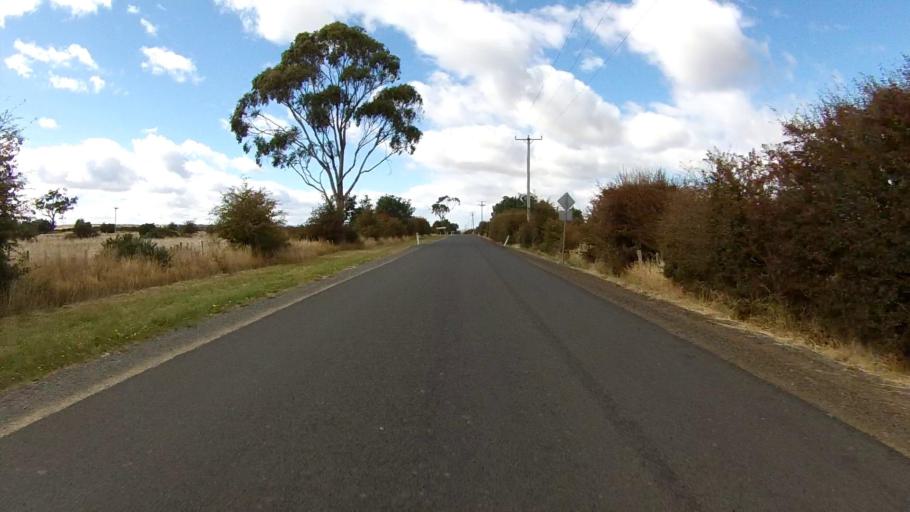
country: AU
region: Tasmania
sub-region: Northern Midlands
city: Evandale
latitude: -41.6534
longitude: 147.3325
